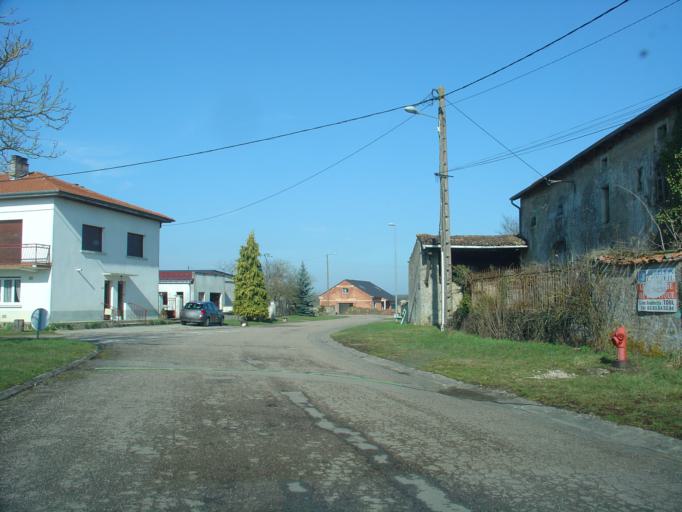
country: FR
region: Lorraine
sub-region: Departement de Meurthe-et-Moselle
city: Villey-Saint-Etienne
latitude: 48.7840
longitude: 5.9239
